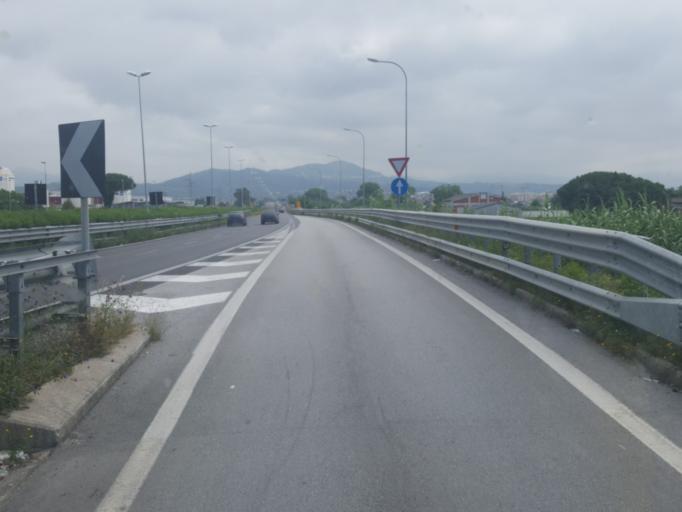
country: IT
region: Campania
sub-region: Provincia di Salerno
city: Fuorni
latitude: 40.6371
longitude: 14.8577
